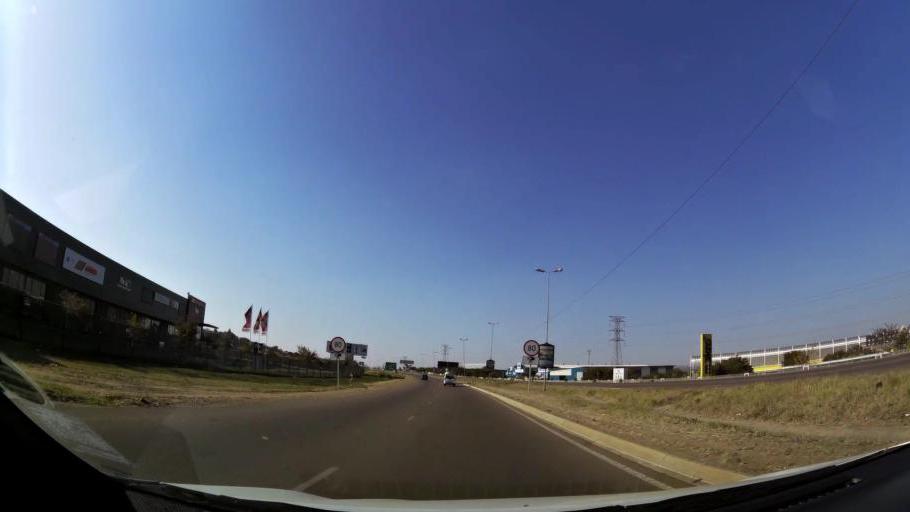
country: ZA
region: Gauteng
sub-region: City of Tshwane Metropolitan Municipality
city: Pretoria
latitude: -25.7744
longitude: 28.3509
